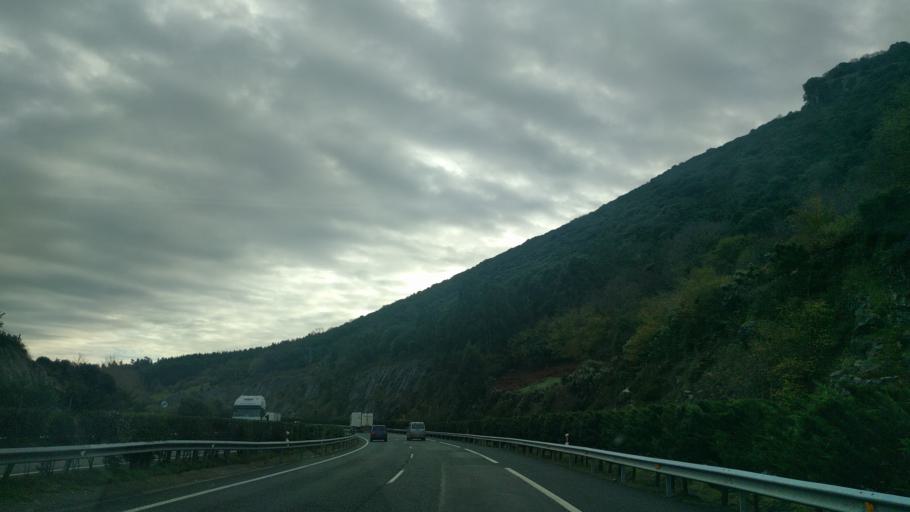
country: ES
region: Cantabria
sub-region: Provincia de Cantabria
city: Castro-Urdiales
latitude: 43.3989
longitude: -3.2792
